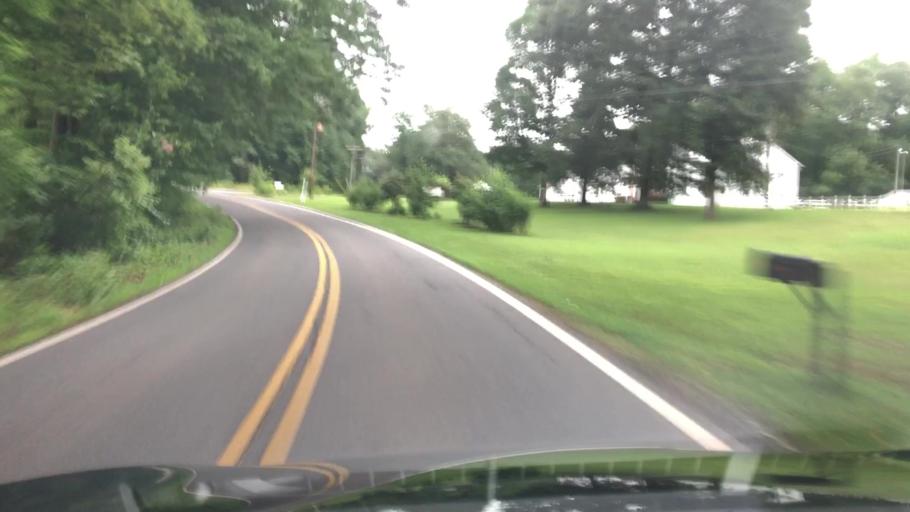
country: US
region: Virginia
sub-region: Fauquier County
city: Bealeton
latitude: 38.4979
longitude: -77.6020
